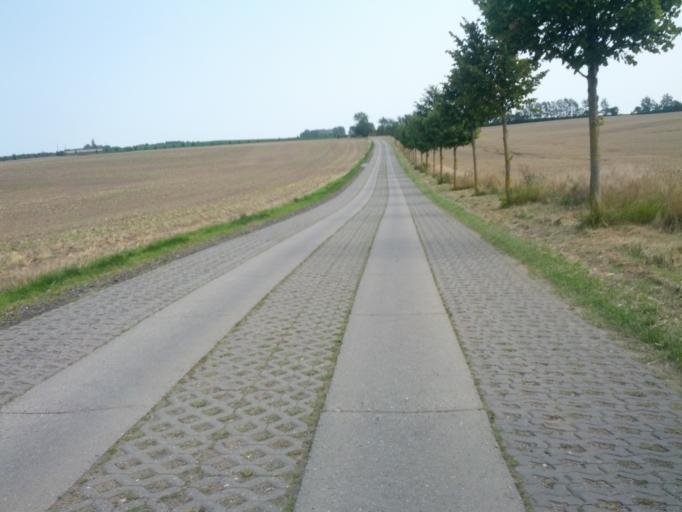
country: DE
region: Mecklenburg-Vorpommern
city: Bastorf
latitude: 54.1300
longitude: 11.6726
